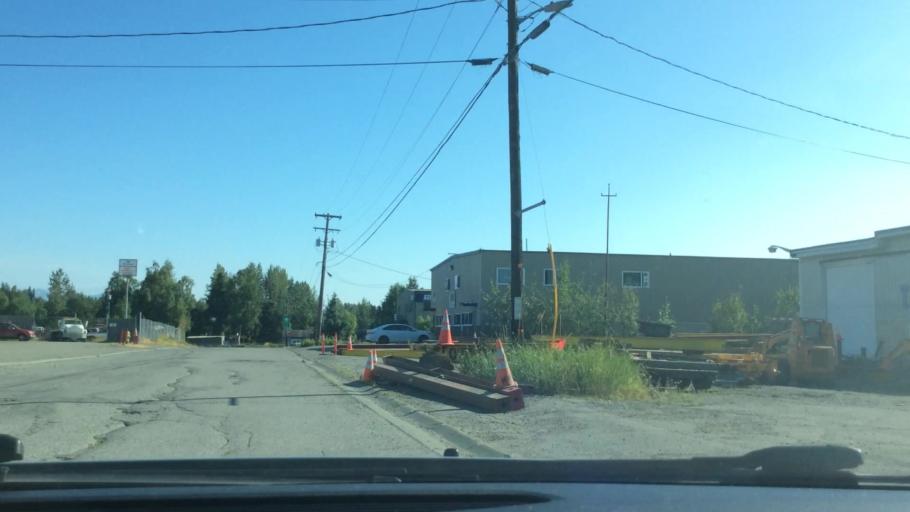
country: US
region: Alaska
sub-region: Anchorage Municipality
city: Anchorage
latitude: 61.1641
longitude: -149.8461
